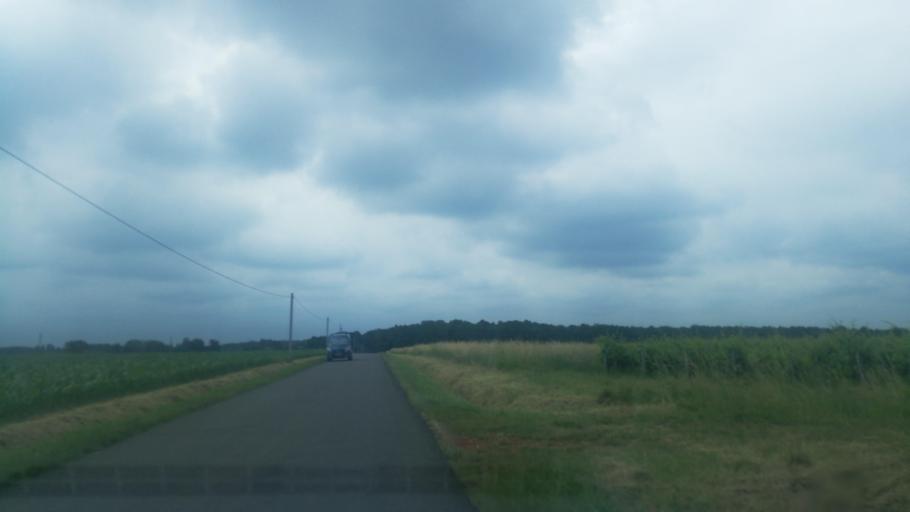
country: FR
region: Centre
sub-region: Departement du Loir-et-Cher
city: Saint-Romain-sur-Cher
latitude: 47.3438
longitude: 1.4477
